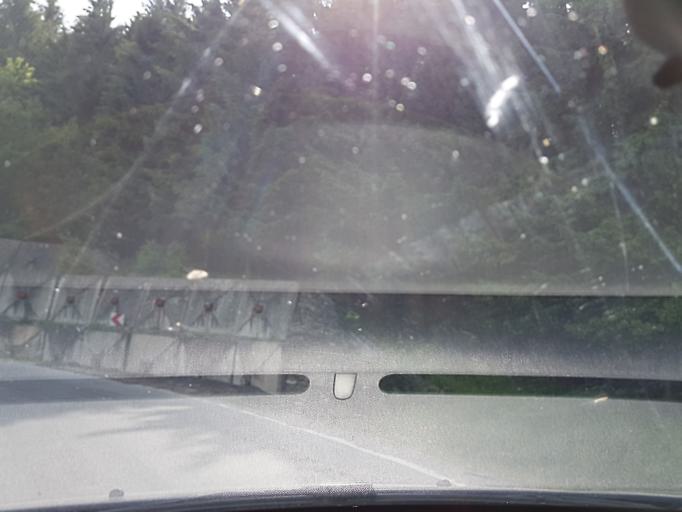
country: RO
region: Prahova
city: Maneciu
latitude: 45.3337
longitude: 25.9664
